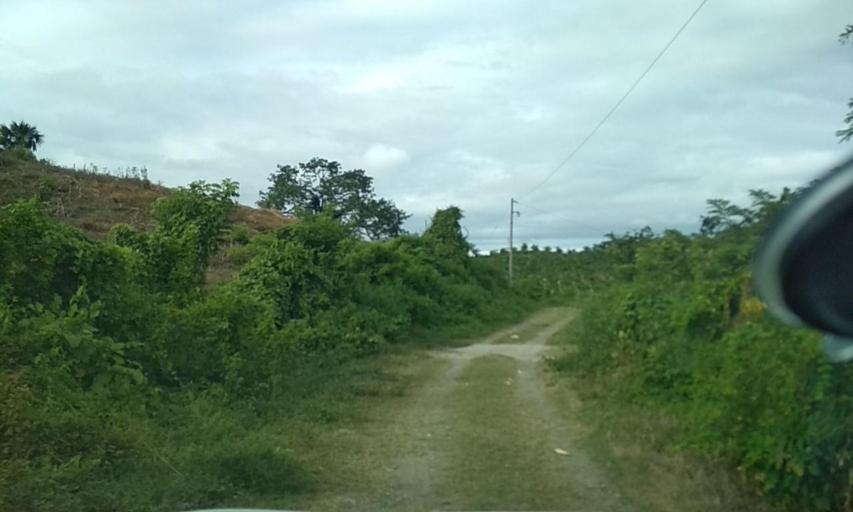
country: MX
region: Veracruz
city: Cazones de Herrera
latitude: 20.6511
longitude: -97.3367
